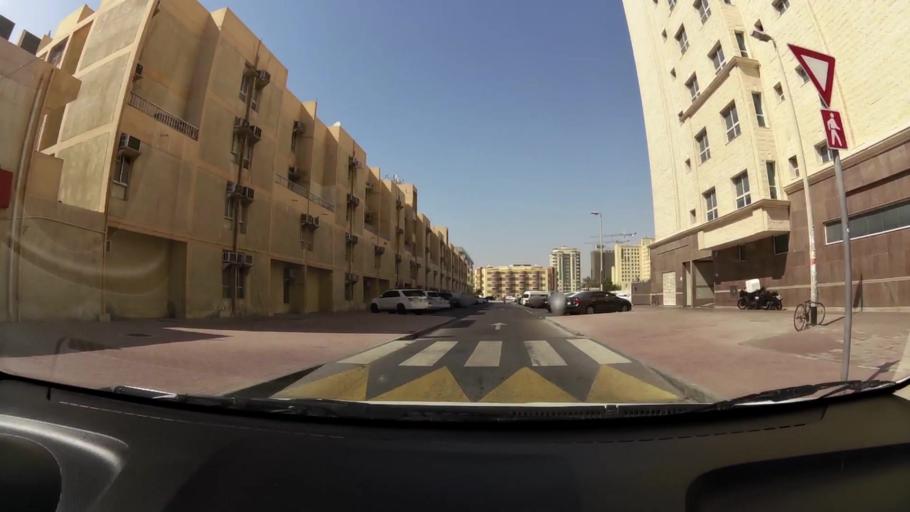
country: AE
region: Ash Shariqah
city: Sharjah
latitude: 25.2693
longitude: 55.3767
